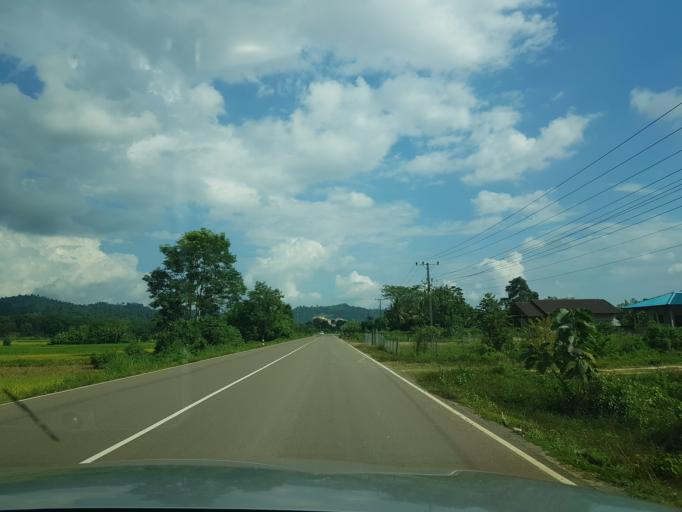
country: TH
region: Nong Khai
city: Sangkhom
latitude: 18.1490
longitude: 102.2084
